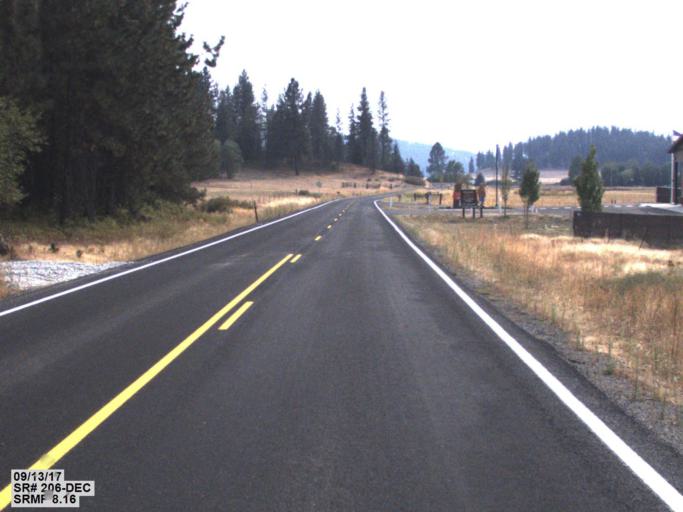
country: US
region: Washington
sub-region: Spokane County
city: Trentwood
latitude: 47.8197
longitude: -117.2123
